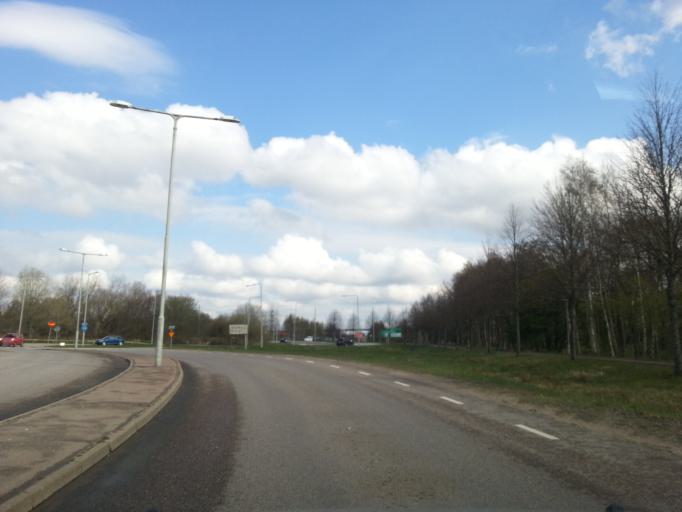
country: SE
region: Vaestra Goetaland
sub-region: Goteborg
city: Gardsten
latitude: 57.7855
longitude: 12.0020
